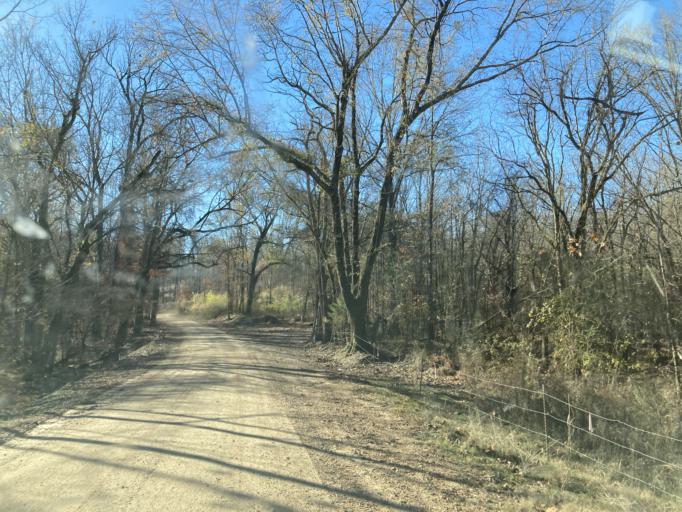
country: US
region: Mississippi
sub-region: Yazoo County
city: Yazoo City
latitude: 32.7113
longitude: -90.4162
